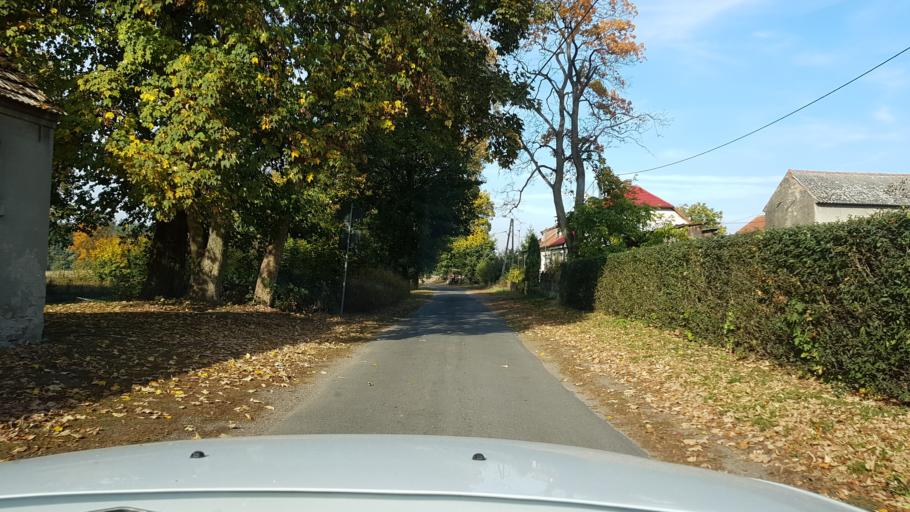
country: PL
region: West Pomeranian Voivodeship
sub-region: Powiat mysliborski
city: Mysliborz
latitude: 52.9313
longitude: 14.9410
